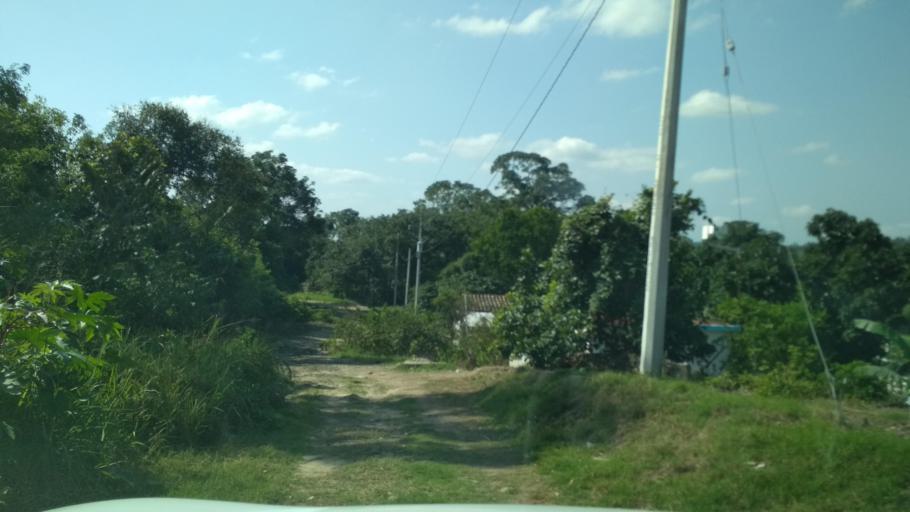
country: MX
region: Puebla
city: San Jose Acateno
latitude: 20.1891
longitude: -97.1551
